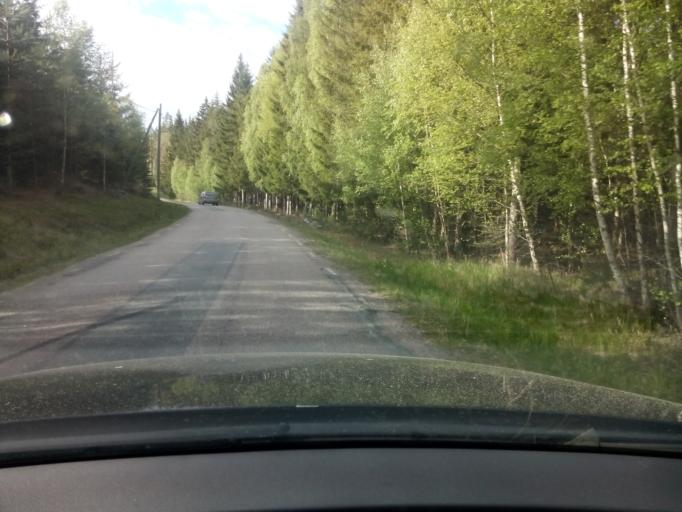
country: SE
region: Soedermanland
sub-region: Nykopings Kommun
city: Stigtomta
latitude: 58.9071
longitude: 16.8838
